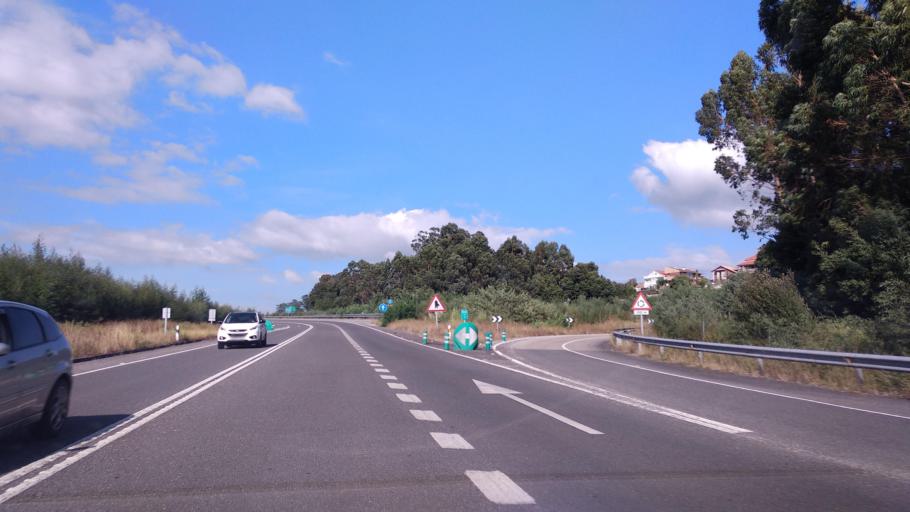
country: ES
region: Galicia
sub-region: Provincia de Pontevedra
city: Moana
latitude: 42.2768
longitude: -8.7547
